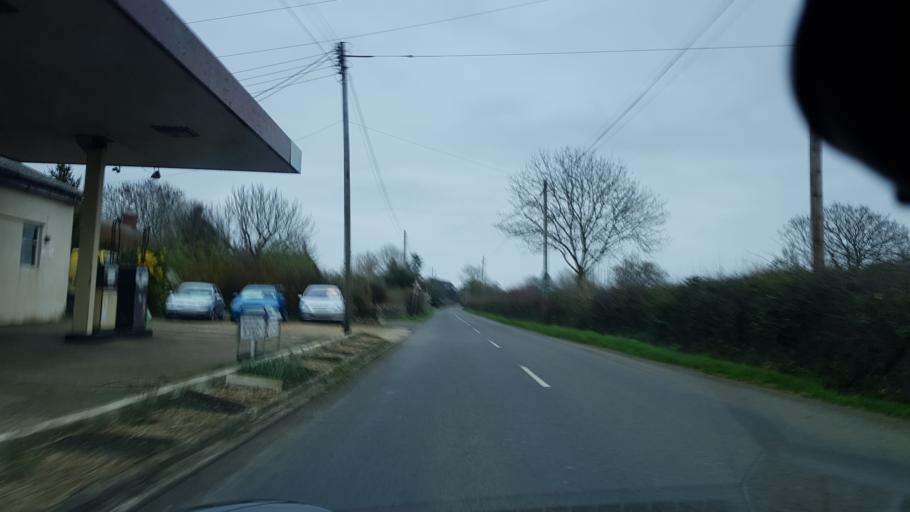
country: GB
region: England
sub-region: Somerset
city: Ilminster
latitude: 50.9487
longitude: -2.9281
